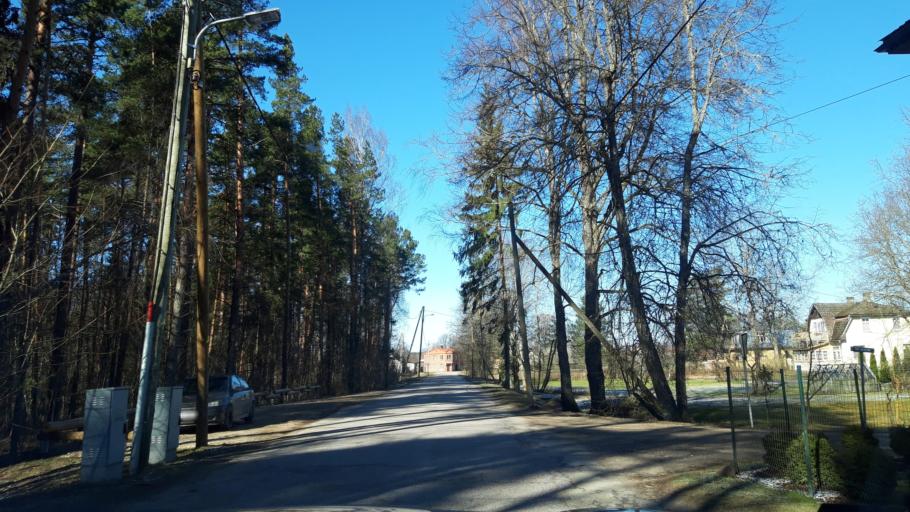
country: LV
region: Strenci
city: Strenci
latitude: 57.6224
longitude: 25.6967
